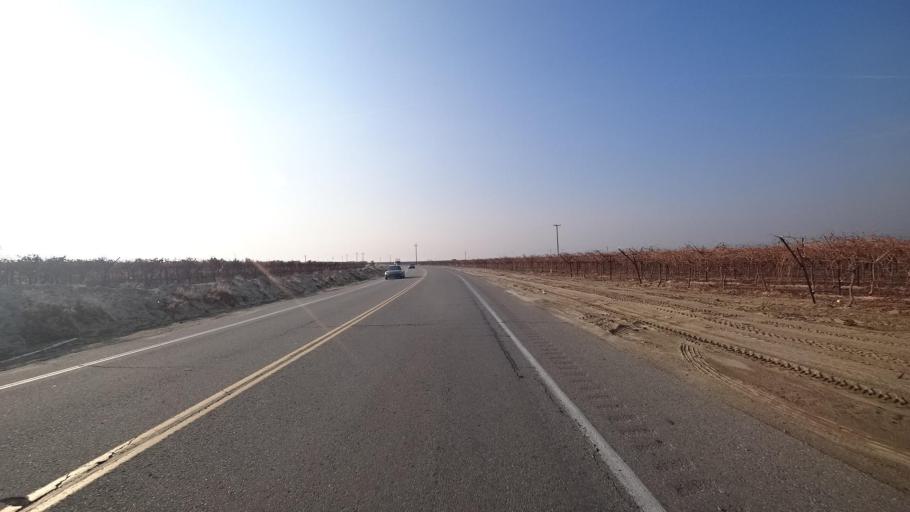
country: US
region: California
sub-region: Kern County
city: Arvin
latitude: 35.0884
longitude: -118.9166
